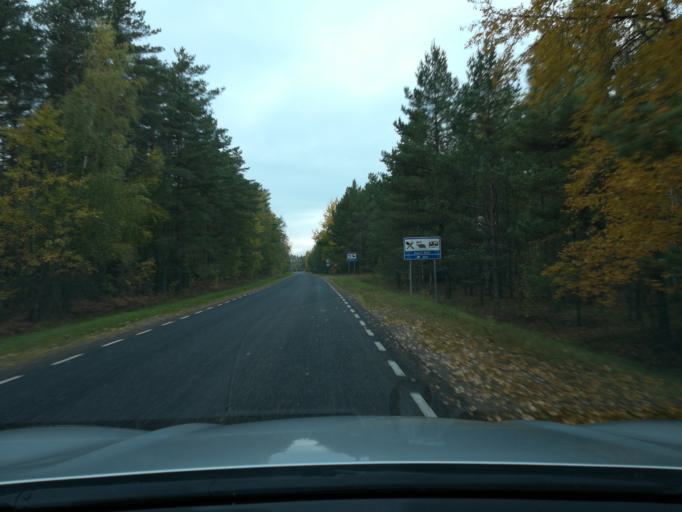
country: EE
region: Ida-Virumaa
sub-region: Johvi vald
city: Johvi
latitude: 59.0137
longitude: 27.4192
